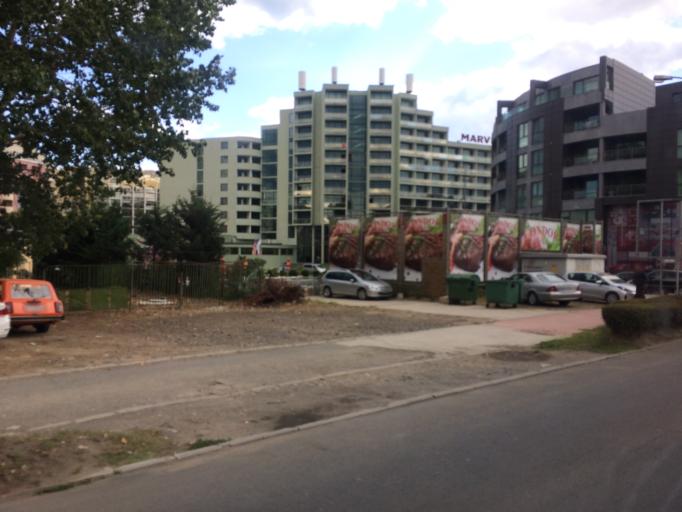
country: BG
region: Burgas
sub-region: Obshtina Nesebur
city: Sveti Vlas
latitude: 42.7093
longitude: 27.7239
